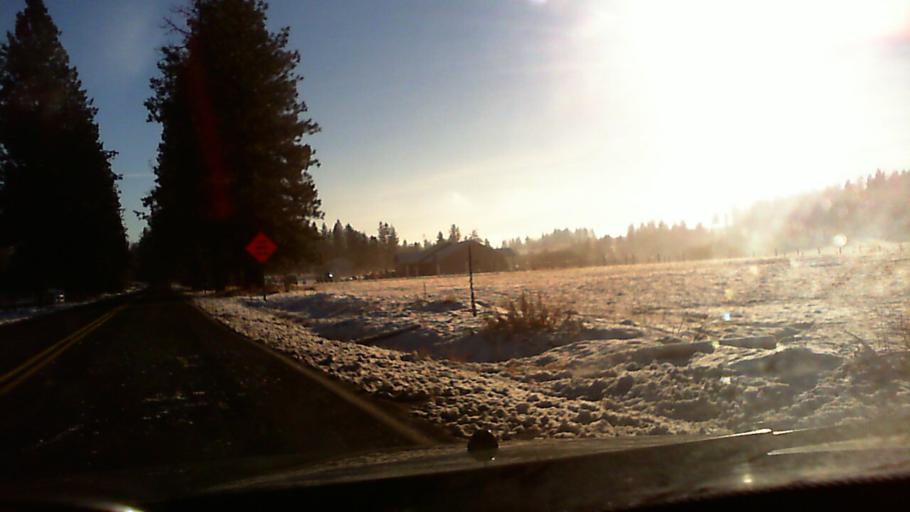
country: US
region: Washington
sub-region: Spokane County
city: Trentwood
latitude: 47.7285
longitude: -117.2131
